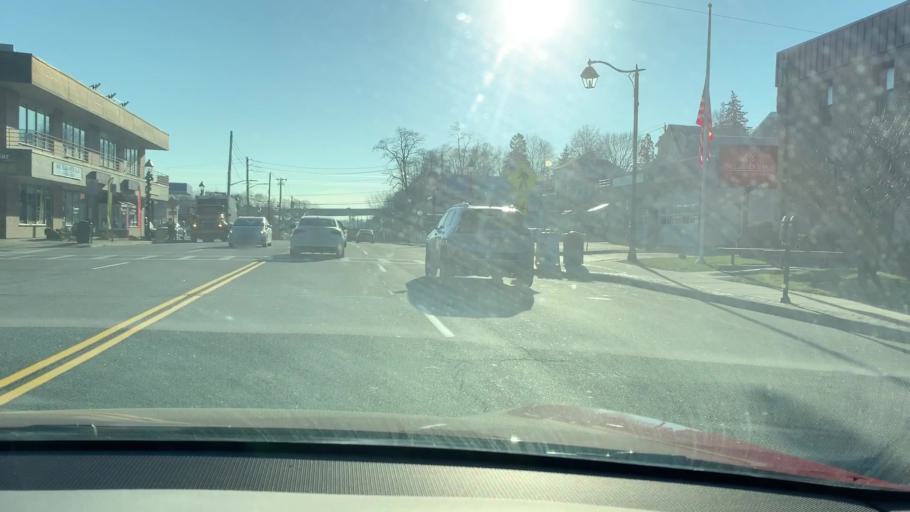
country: US
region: New York
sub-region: Westchester County
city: Elmsford
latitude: 41.0534
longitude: -73.8162
